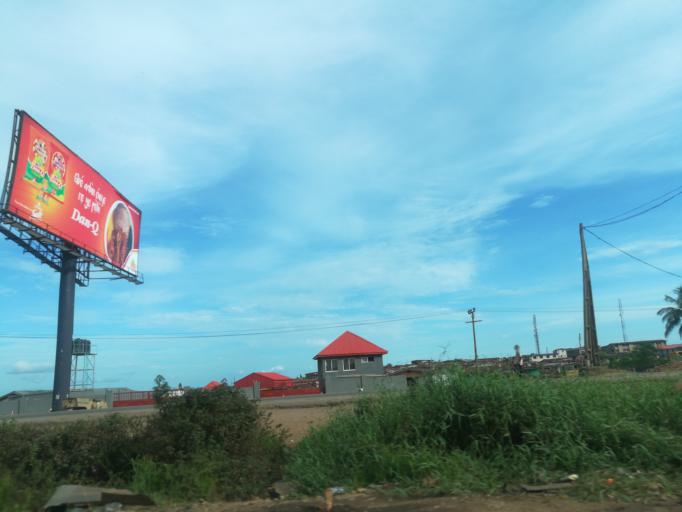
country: NG
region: Oyo
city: Ibadan
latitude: 7.3675
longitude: 3.9273
